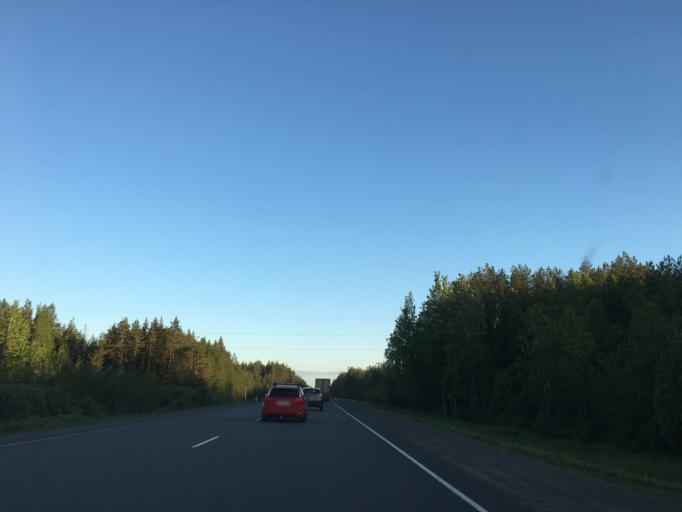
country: RU
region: Leningrad
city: Rozhdestveno
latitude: 59.2983
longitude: 29.9411
